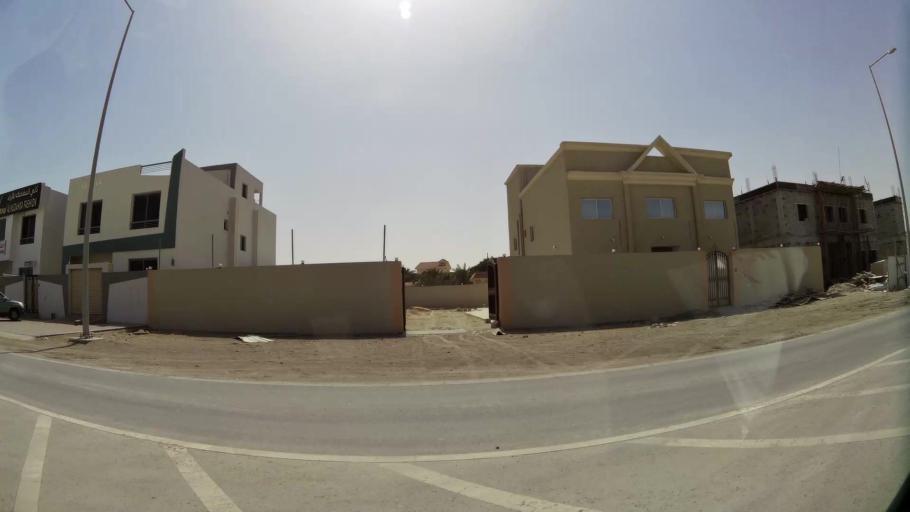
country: QA
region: Baladiyat Umm Salal
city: Umm Salal Muhammad
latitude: 25.3721
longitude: 51.4407
